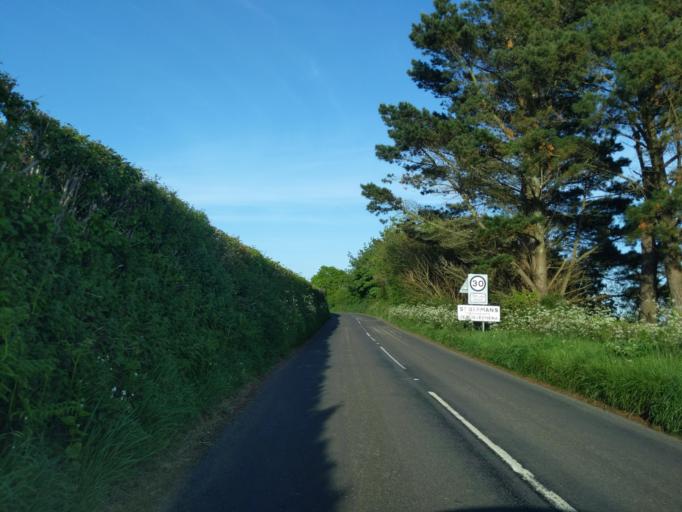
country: GB
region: England
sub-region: Cornwall
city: Pillaton
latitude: 50.3932
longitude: -4.3148
